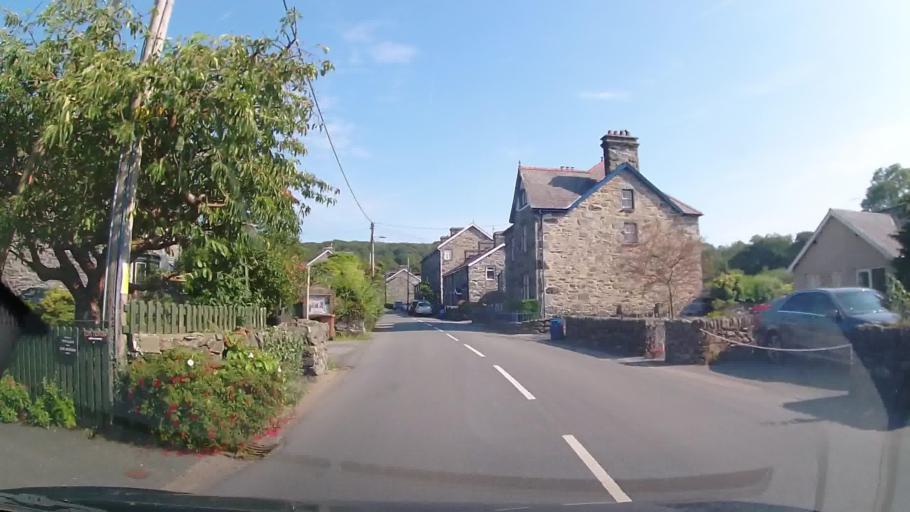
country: GB
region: Wales
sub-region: Gwynedd
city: Llanbedr
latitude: 52.8219
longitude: -4.1022
